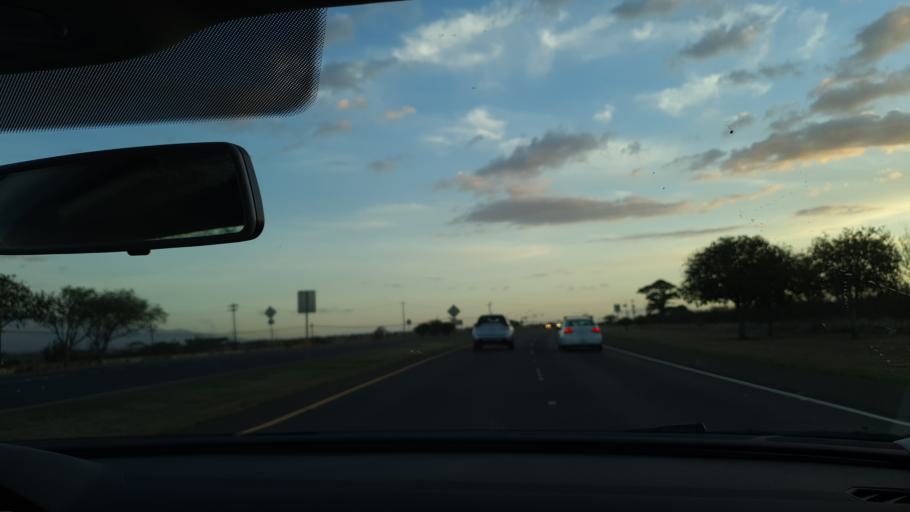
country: US
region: Hawaii
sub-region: Maui County
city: Kahului
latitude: 20.8670
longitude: -156.4571
